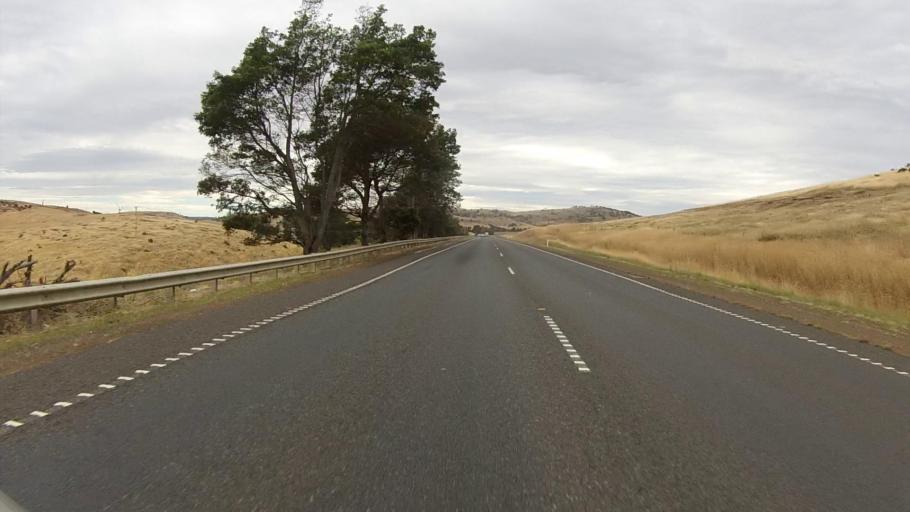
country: AU
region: Tasmania
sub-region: Brighton
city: Bridgewater
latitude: -42.3768
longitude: 147.3258
